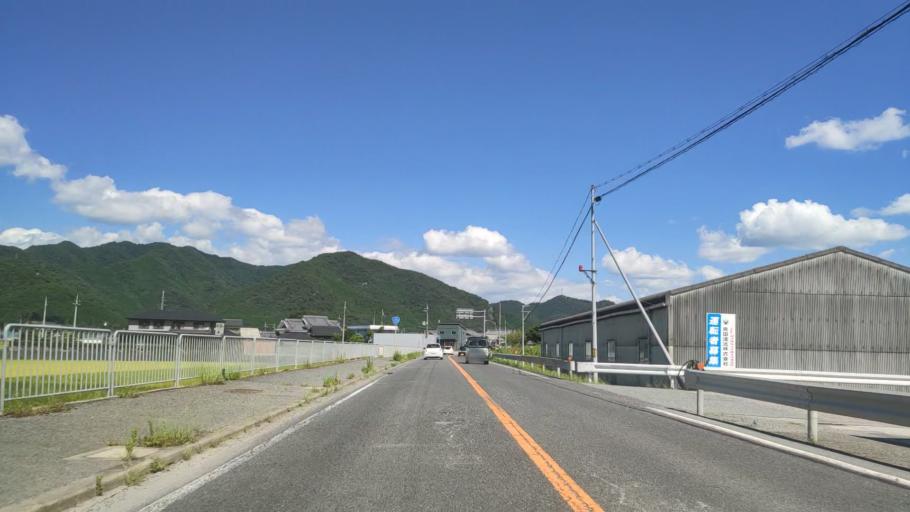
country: JP
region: Hyogo
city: Nishiwaki
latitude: 35.0415
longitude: 134.9846
